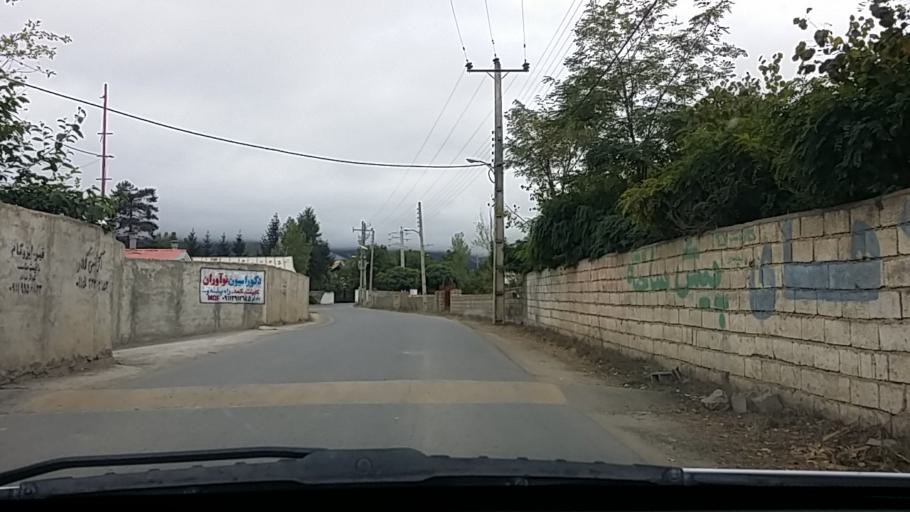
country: IR
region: Mazandaran
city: `Abbasabad
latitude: 36.5275
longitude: 51.1756
